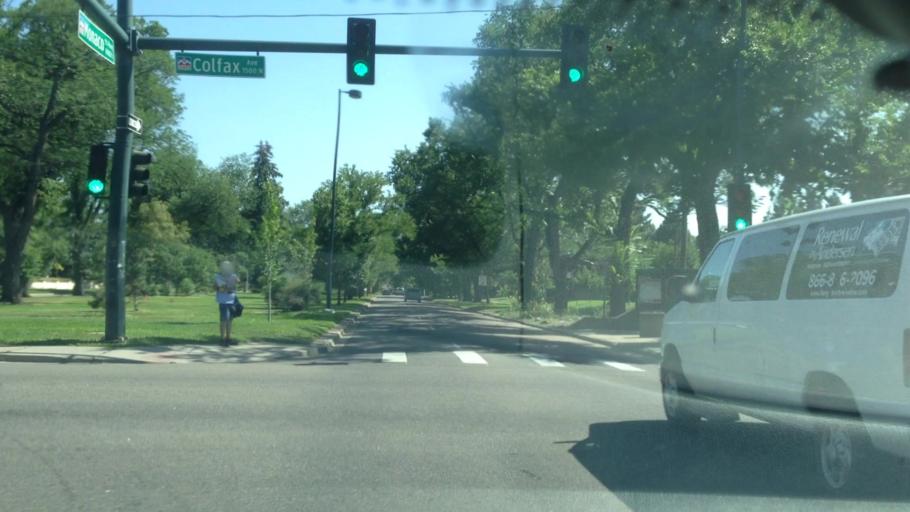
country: US
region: Colorado
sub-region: Arapahoe County
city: Glendale
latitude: 39.7402
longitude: -104.9128
